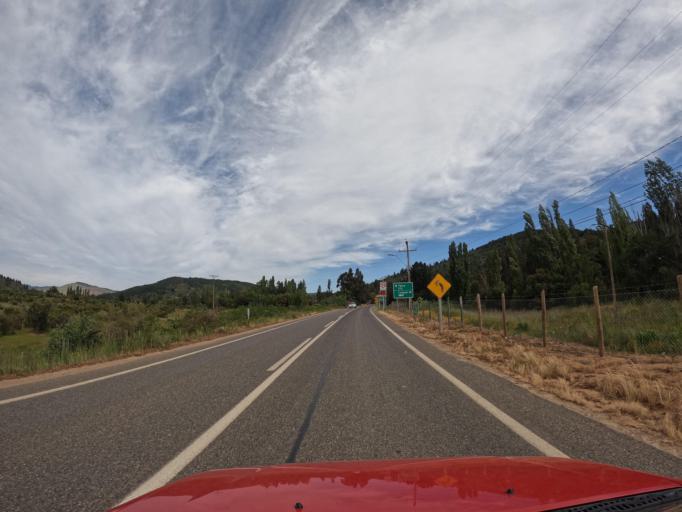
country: CL
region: Maule
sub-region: Provincia de Talca
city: Talca
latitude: -35.3180
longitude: -71.9589
